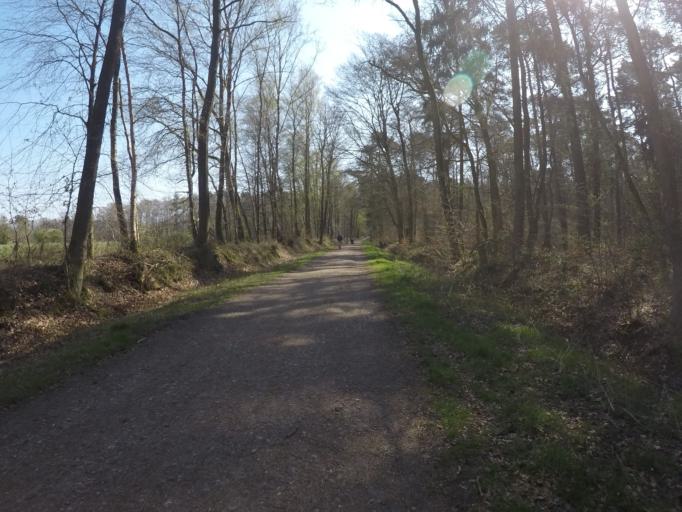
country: DE
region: Schleswig-Holstein
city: Rellingen
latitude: 53.6141
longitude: 9.7777
